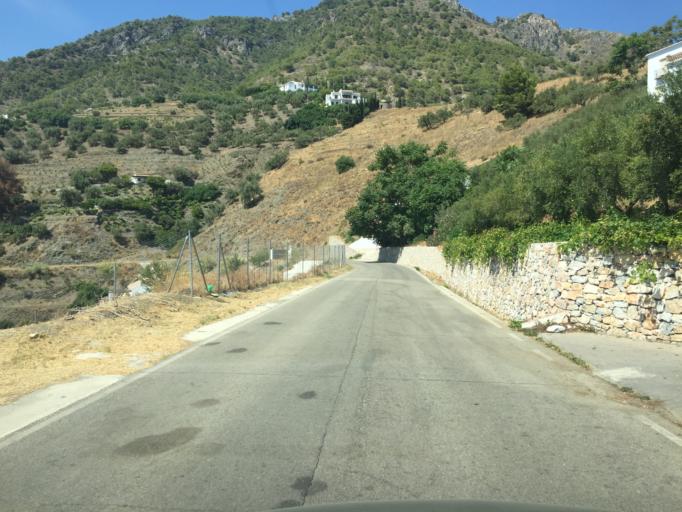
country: ES
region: Andalusia
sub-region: Provincia de Malaga
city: Frigiliana
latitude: 36.8032
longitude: -3.9196
